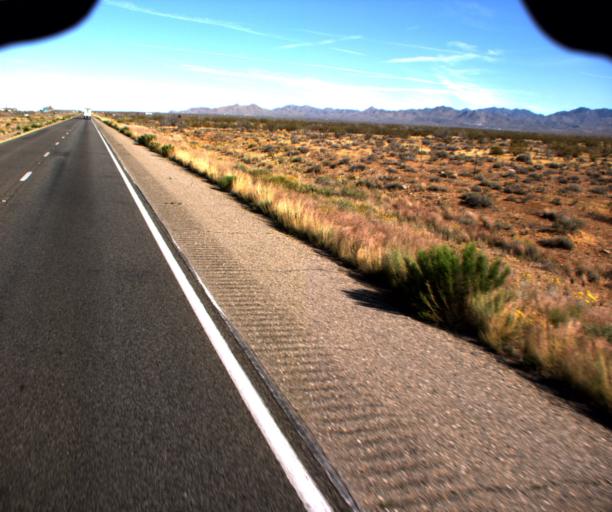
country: US
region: Arizona
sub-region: Mohave County
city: Golden Valley
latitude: 35.3263
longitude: -114.2081
